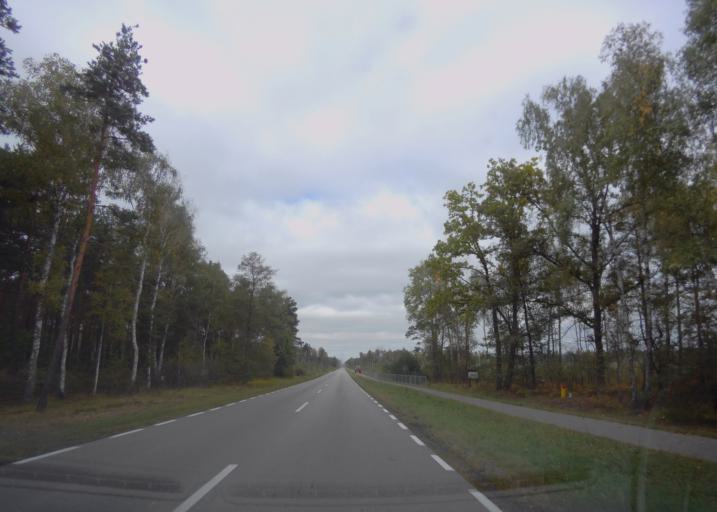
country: PL
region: Lublin Voivodeship
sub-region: Powiat wlodawski
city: Wlodawa
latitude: 51.4773
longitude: 23.5144
